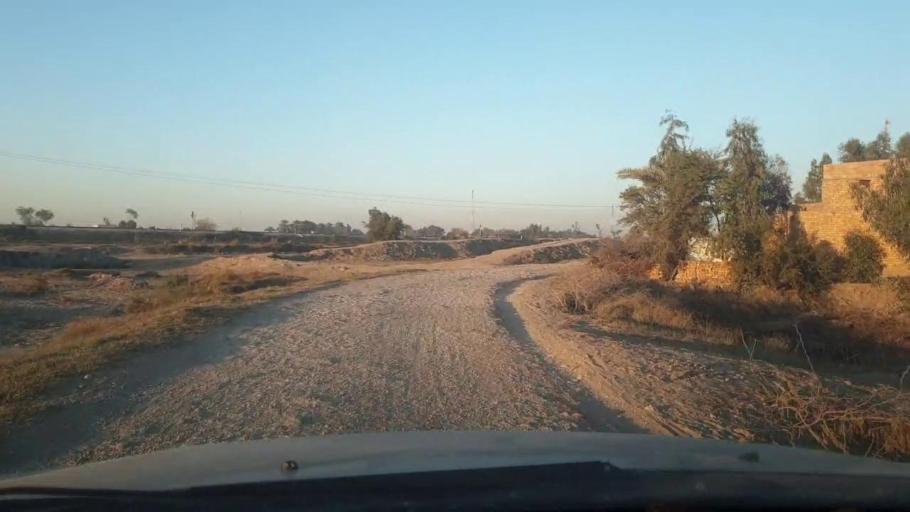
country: PK
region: Sindh
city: Pano Aqil
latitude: 27.9167
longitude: 69.1939
